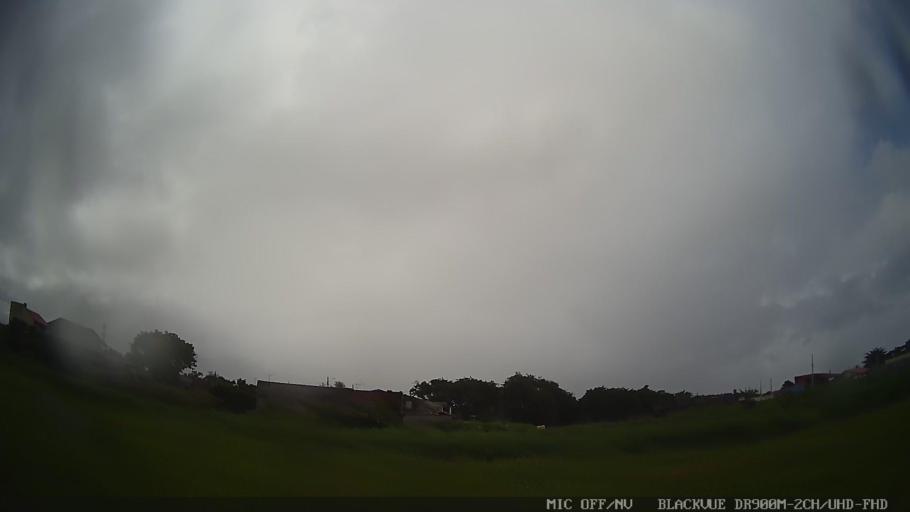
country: BR
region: Sao Paulo
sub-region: Itanhaem
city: Itanhaem
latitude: -24.2152
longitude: -46.8653
